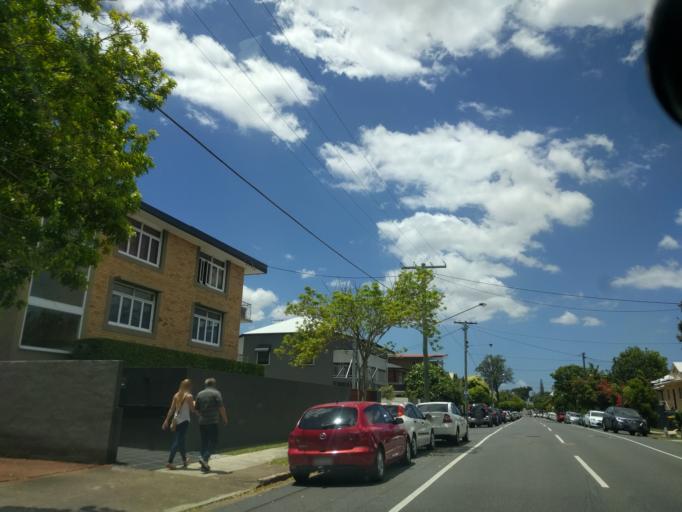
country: AU
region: Queensland
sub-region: Brisbane
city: Fortitude Valley
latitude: -27.4608
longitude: 153.0413
